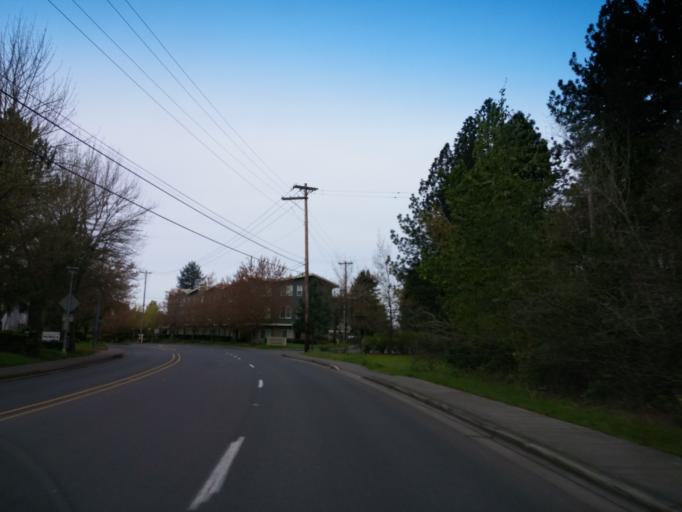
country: US
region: Oregon
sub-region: Washington County
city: Aloha
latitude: 45.5126
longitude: -122.8469
